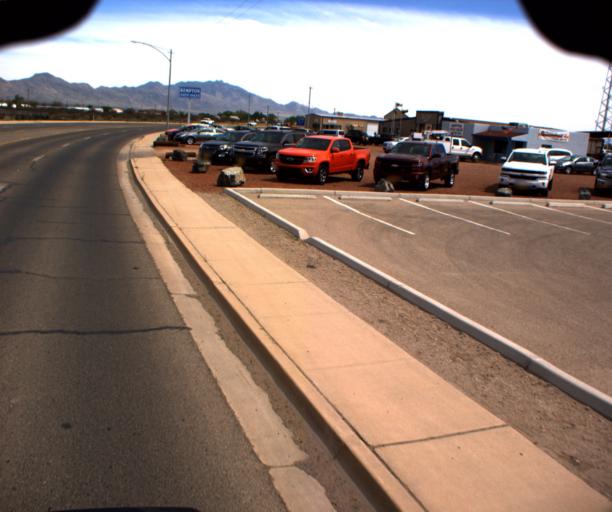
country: US
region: Arizona
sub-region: Cochise County
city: Willcox
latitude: 32.2640
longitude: -109.8324
